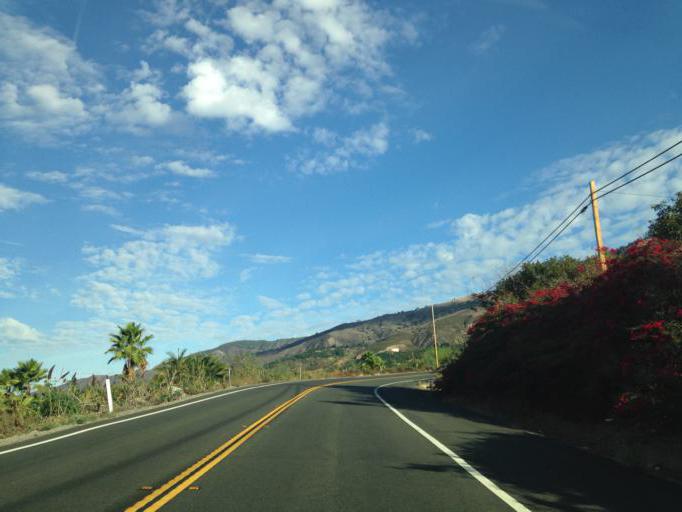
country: US
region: California
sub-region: San Diego County
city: Valley Center
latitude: 33.3007
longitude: -116.9391
